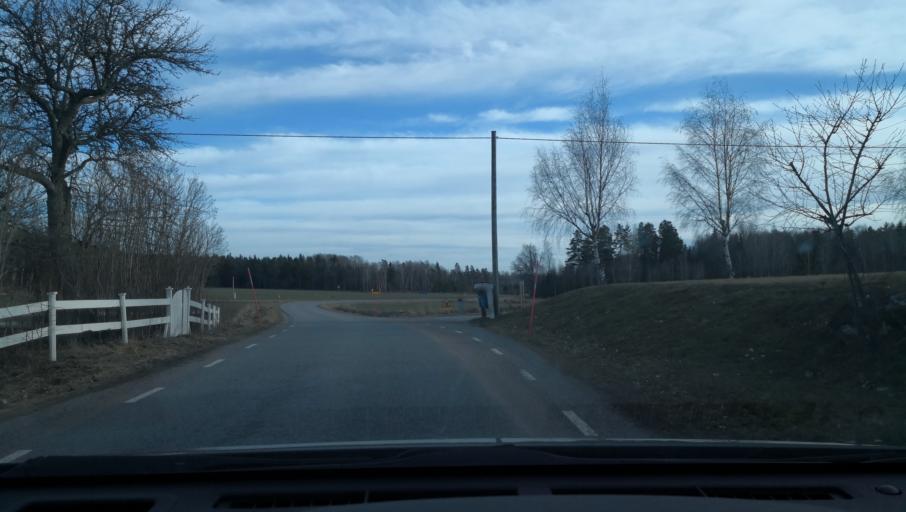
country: SE
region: Uppsala
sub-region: Enkopings Kommun
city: Grillby
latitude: 59.5408
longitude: 17.1644
